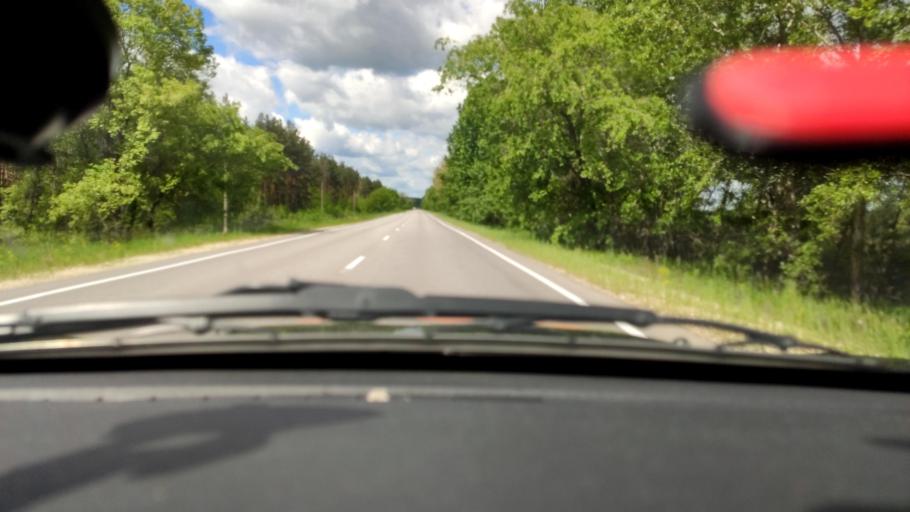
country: RU
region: Belgorod
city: Krasnoye
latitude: 51.0686
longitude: 38.7868
